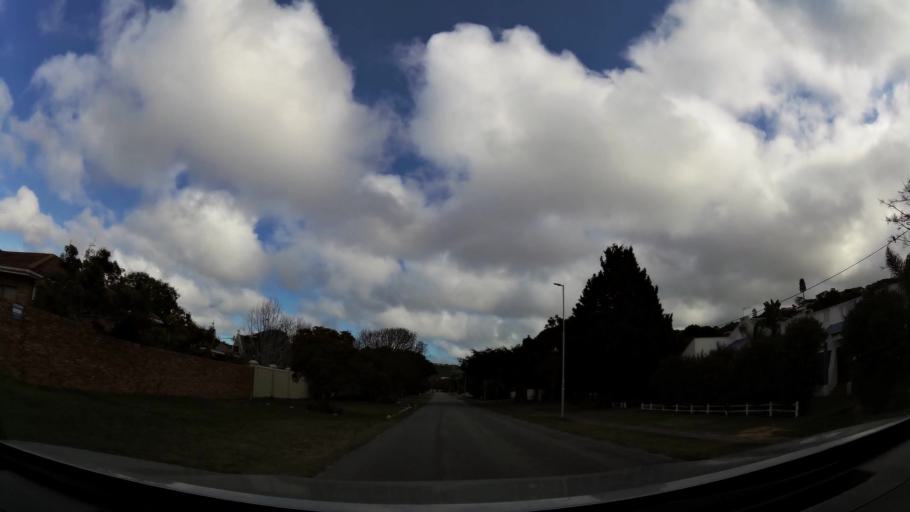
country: ZA
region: Western Cape
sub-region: Eden District Municipality
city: Plettenberg Bay
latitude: -34.0757
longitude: 23.3657
